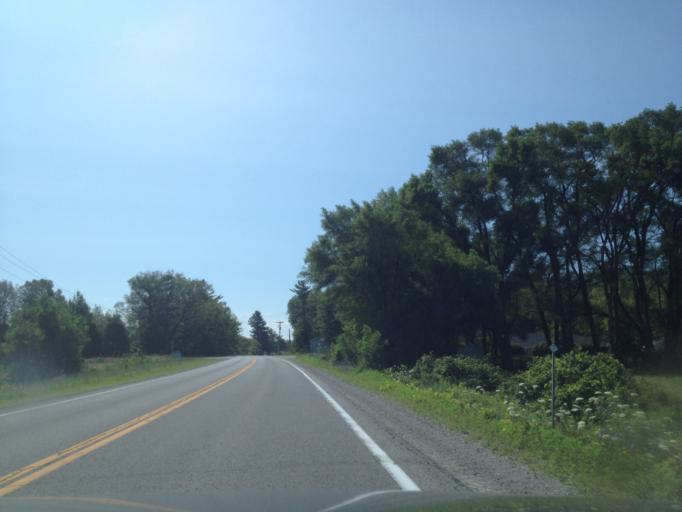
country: CA
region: Ontario
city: Norfolk County
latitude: 42.7762
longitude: -80.3978
